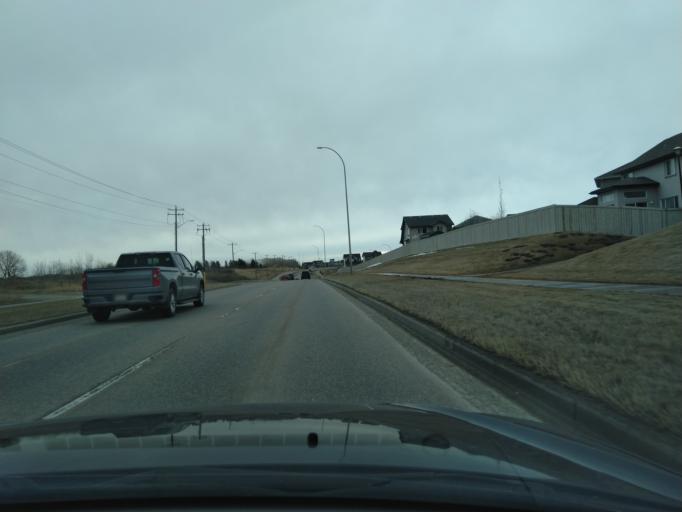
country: CA
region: Alberta
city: Calgary
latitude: 51.1541
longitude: -114.2269
